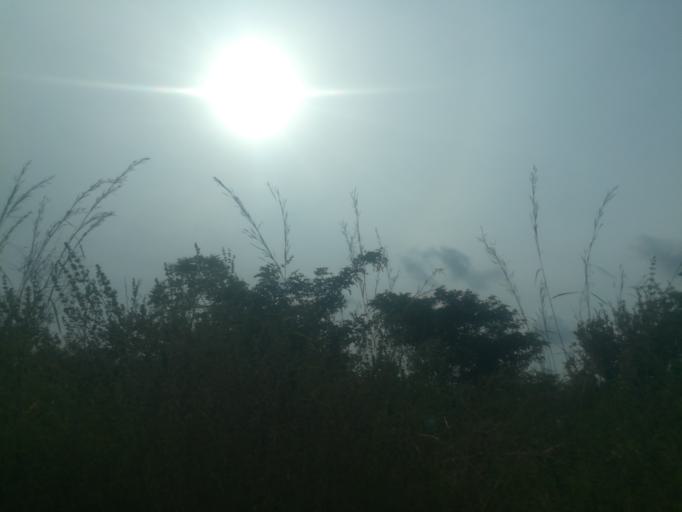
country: NG
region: Ogun
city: Ayetoro
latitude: 7.3202
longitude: 3.0683
